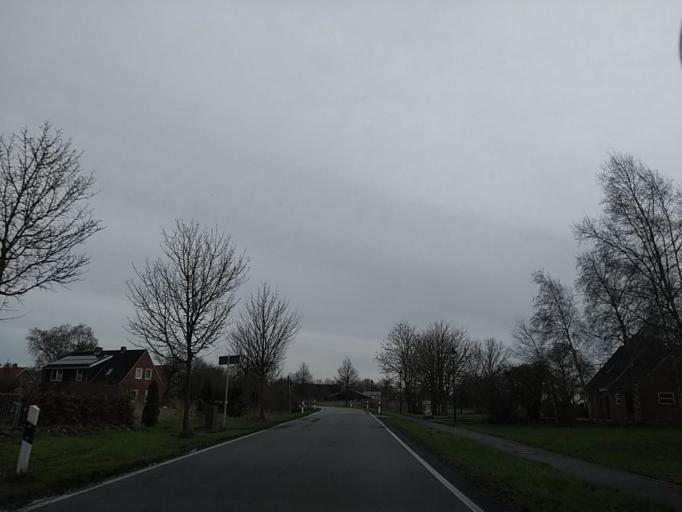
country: DE
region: Lower Saxony
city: Jemgum
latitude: 53.3095
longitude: 7.3091
